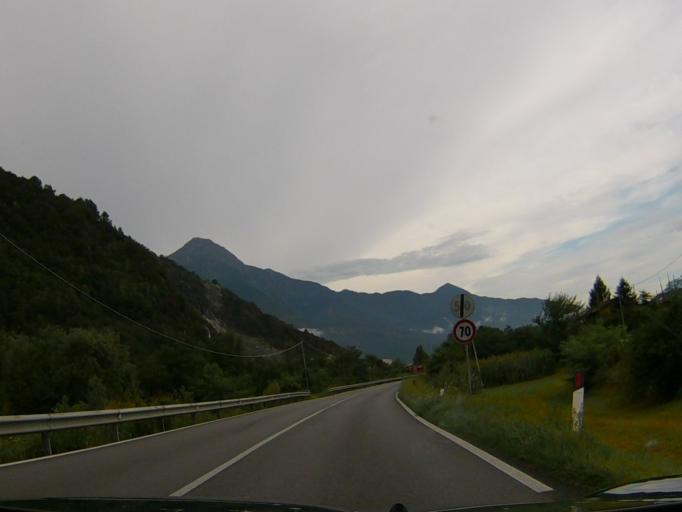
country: IT
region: Lombardy
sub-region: Provincia di Sondrio
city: Verceia
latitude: 46.1842
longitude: 9.4436
